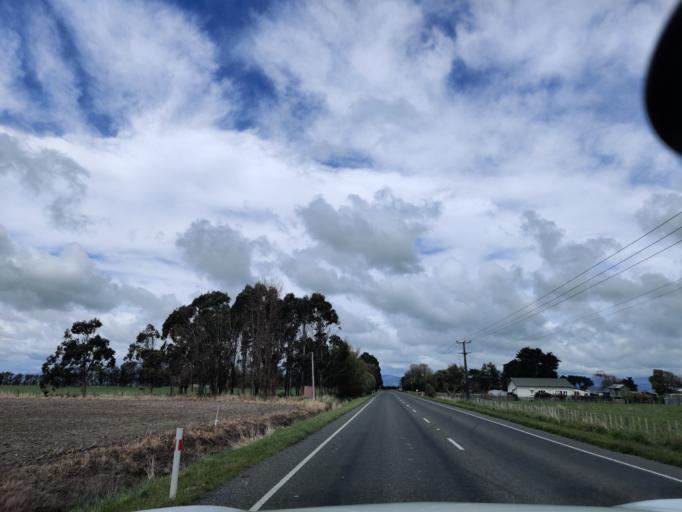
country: NZ
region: Manawatu-Wanganui
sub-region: Palmerston North City
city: Palmerston North
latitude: -40.3247
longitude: 175.5040
